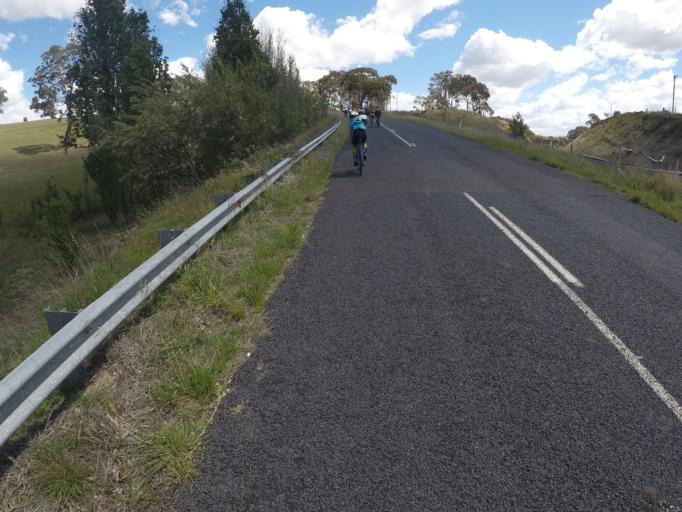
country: AU
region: New South Wales
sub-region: Blayney
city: Blayney
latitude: -33.5795
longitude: 149.4004
